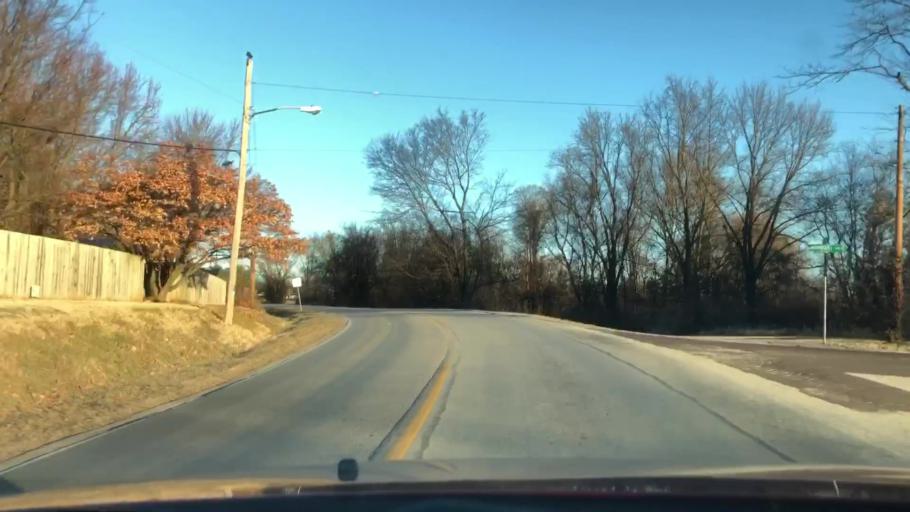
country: US
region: Missouri
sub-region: Greene County
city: Springfield
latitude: 37.1642
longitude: -93.2448
